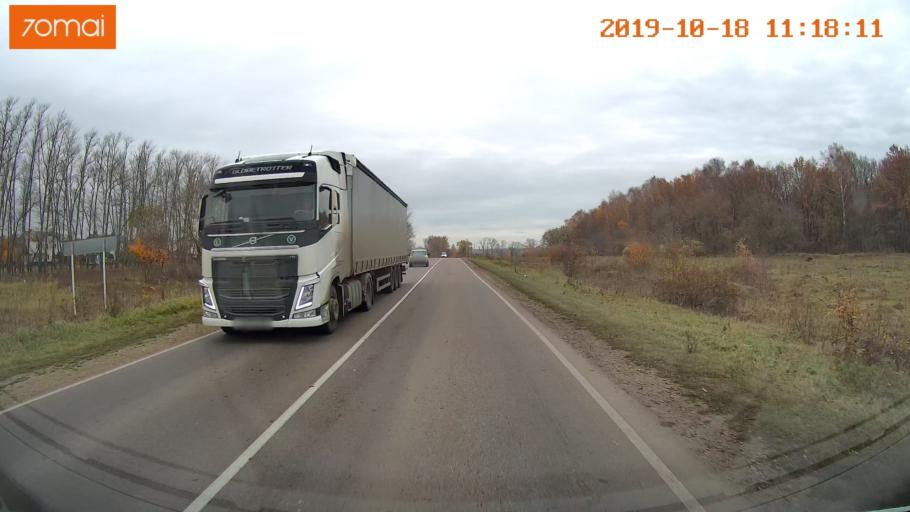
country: RU
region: Tula
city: Kimovsk
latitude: 54.0360
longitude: 38.5504
